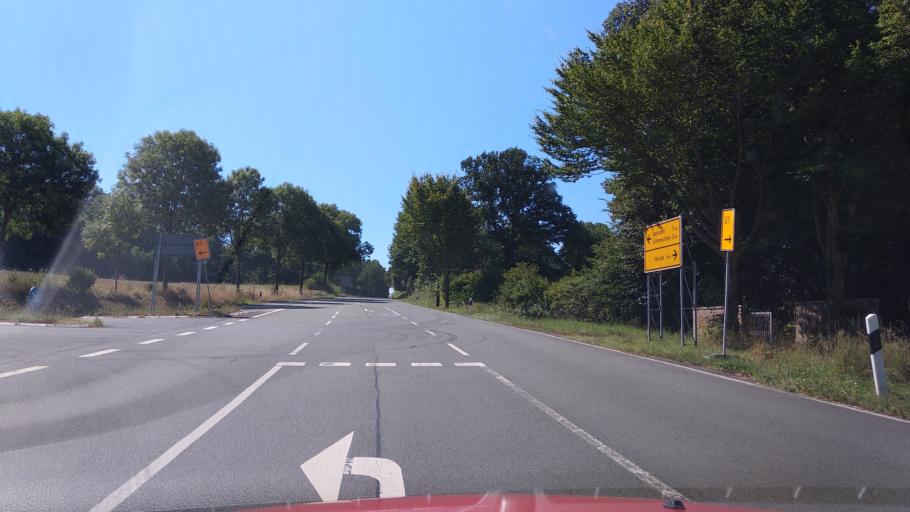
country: DE
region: North Rhine-Westphalia
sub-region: Regierungsbezirk Detmold
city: Bad Driburg
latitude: 51.7040
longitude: 9.0889
